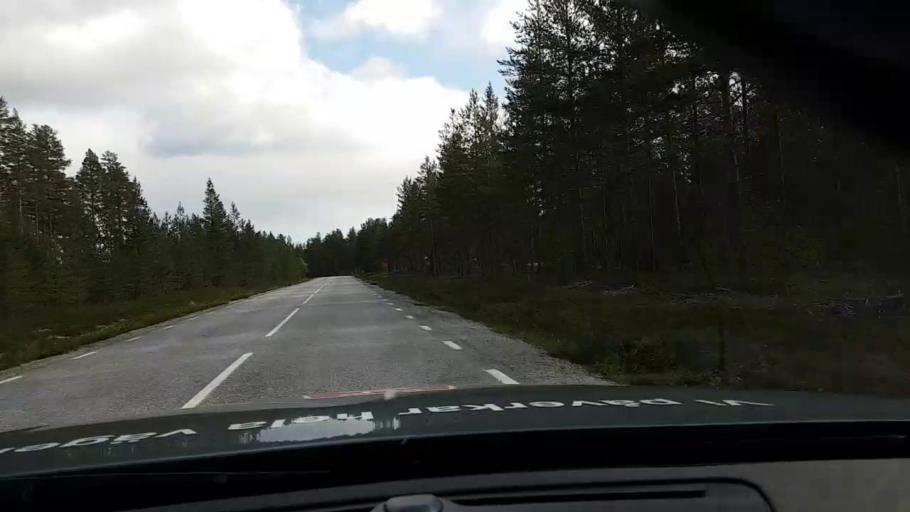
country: SE
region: Vaesternorrland
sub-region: OErnskoeldsviks Kommun
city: Bredbyn
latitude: 63.6750
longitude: 17.7967
